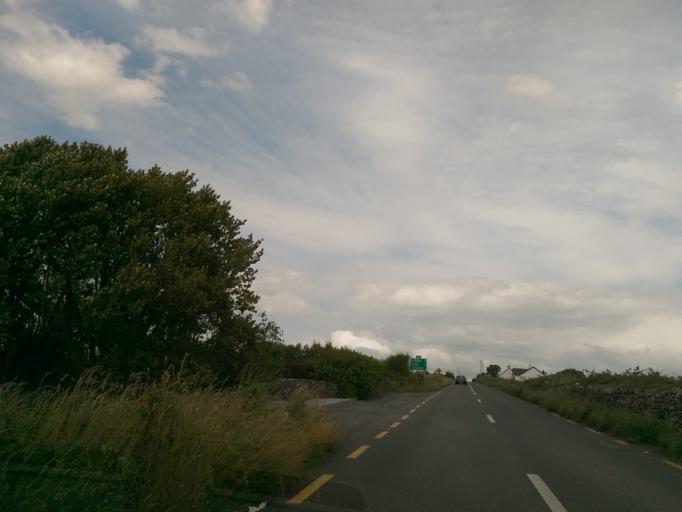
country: IE
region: Munster
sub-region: An Clar
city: Kilrush
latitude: 52.8449
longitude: -9.4207
